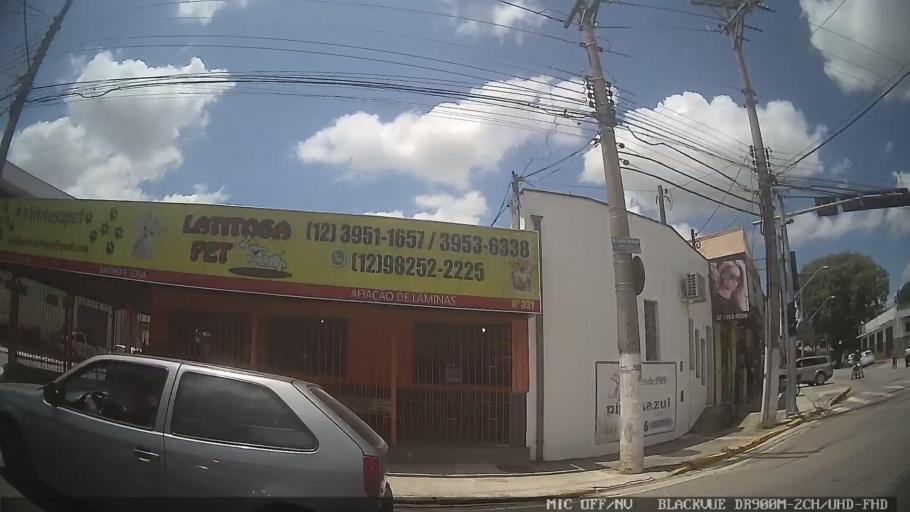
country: BR
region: Sao Paulo
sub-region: Jacarei
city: Jacarei
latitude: -23.3114
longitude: -45.9822
